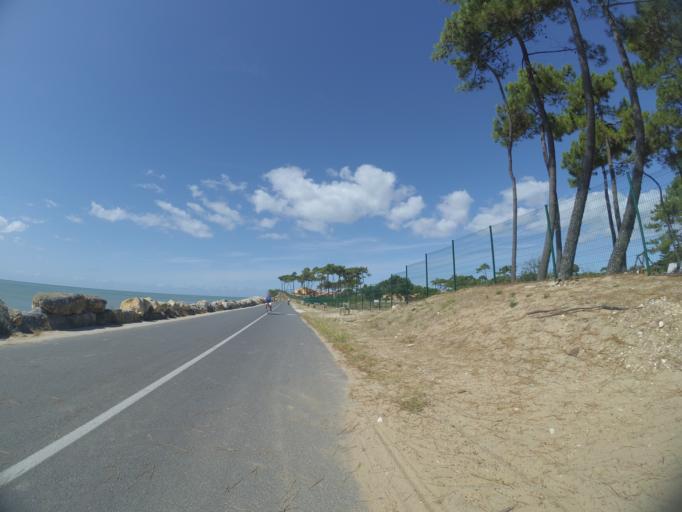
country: FR
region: Poitou-Charentes
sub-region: Departement de la Charente-Maritime
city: Les Mathes
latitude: 45.6760
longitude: -1.1622
